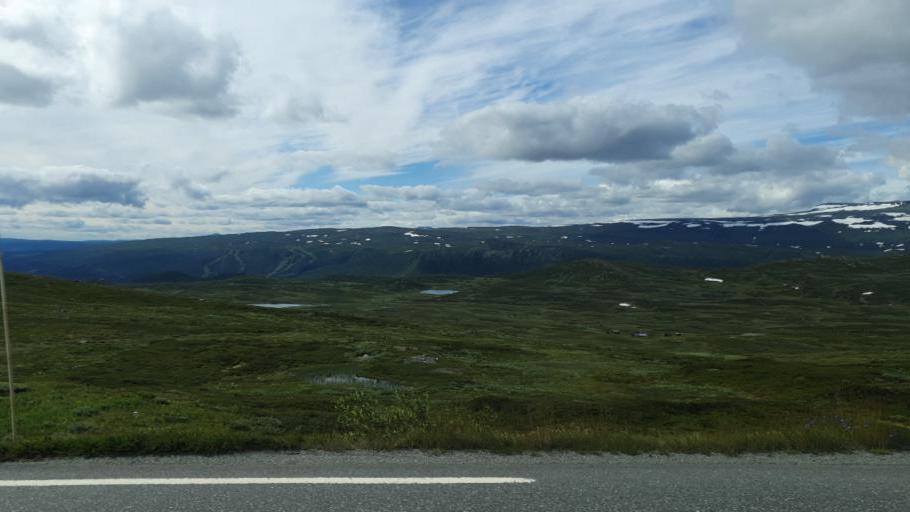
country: NO
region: Oppland
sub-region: Vestre Slidre
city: Slidre
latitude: 61.2864
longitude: 8.8237
